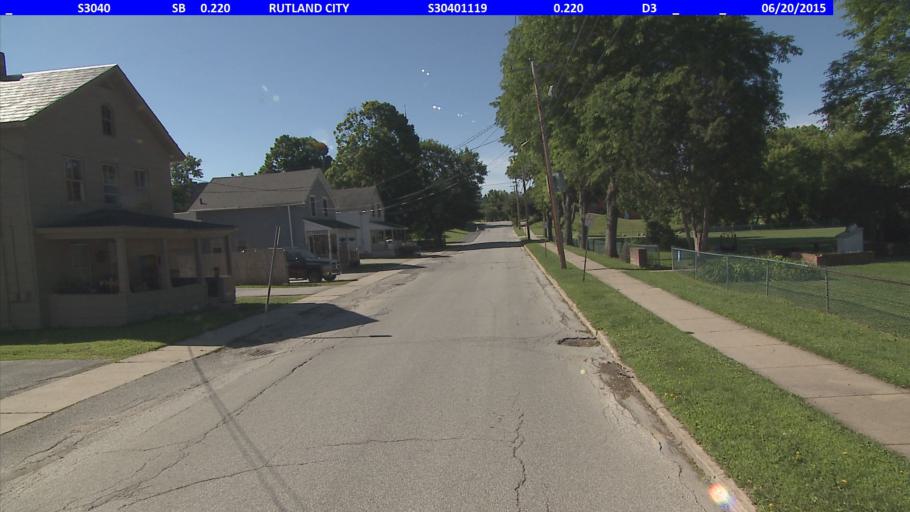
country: US
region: Vermont
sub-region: Rutland County
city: Rutland
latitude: 43.6043
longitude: -72.9866
